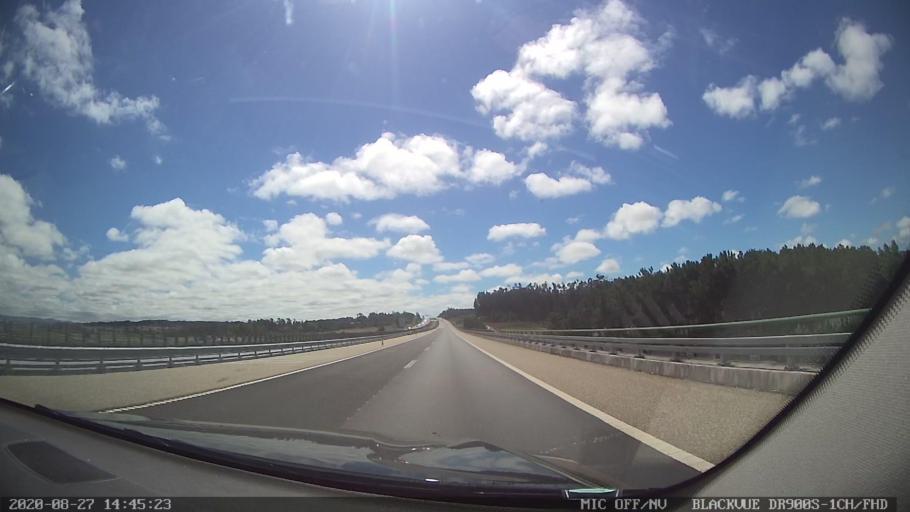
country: PT
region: Leiria
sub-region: Leiria
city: Amor
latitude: 39.8069
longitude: -8.8476
